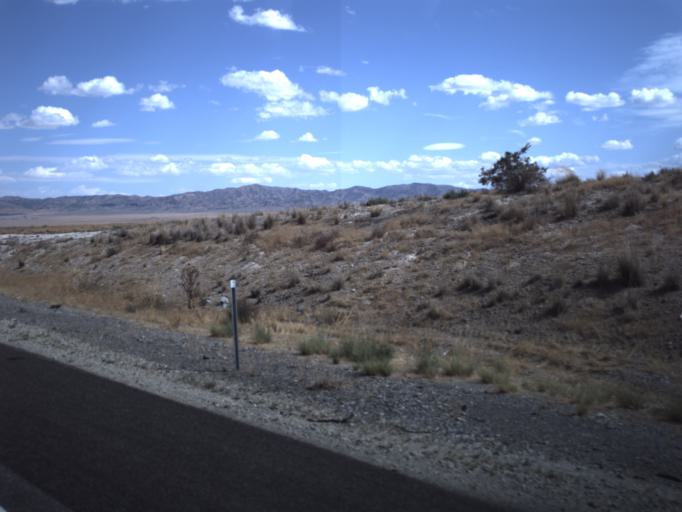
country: US
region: Utah
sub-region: Tooele County
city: Grantsville
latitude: 40.7314
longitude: -113.1139
